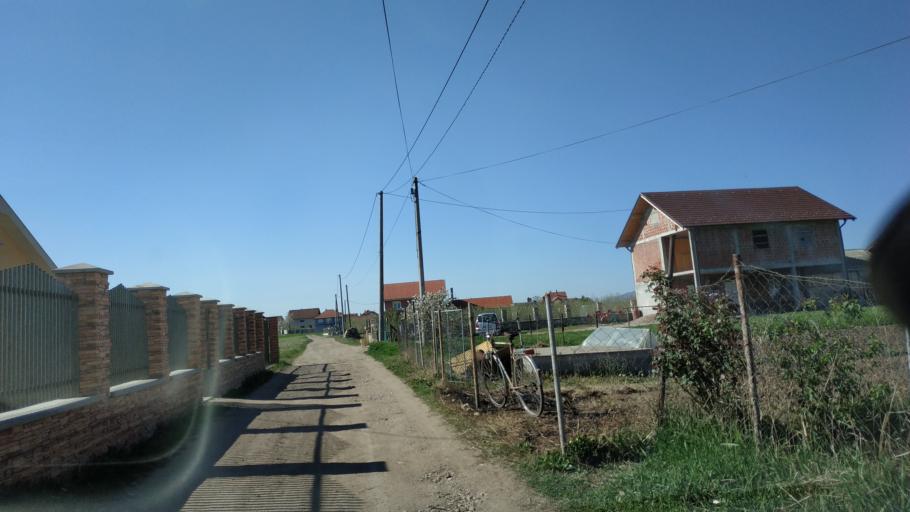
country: RS
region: Central Serbia
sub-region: Nisavski Okrug
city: Aleksinac
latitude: 43.4958
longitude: 21.6973
